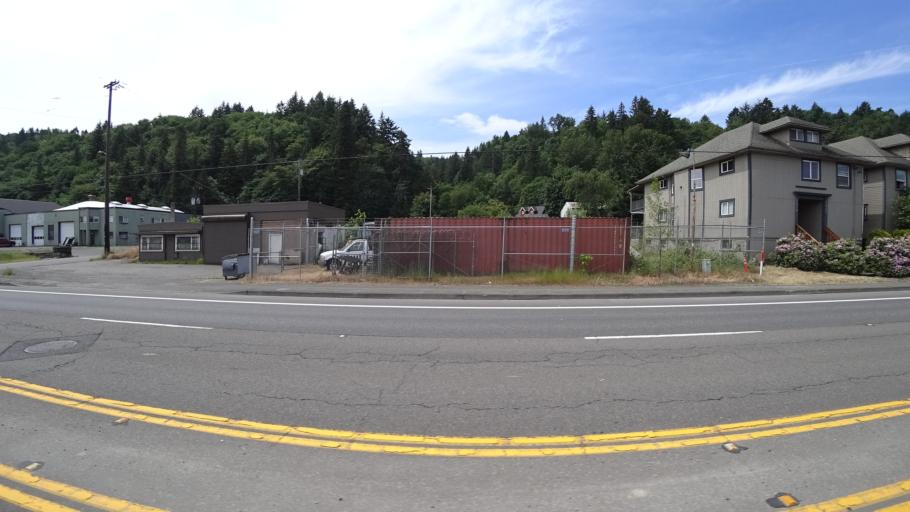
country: US
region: Oregon
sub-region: Washington County
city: West Haven
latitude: 45.5644
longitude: -122.7469
